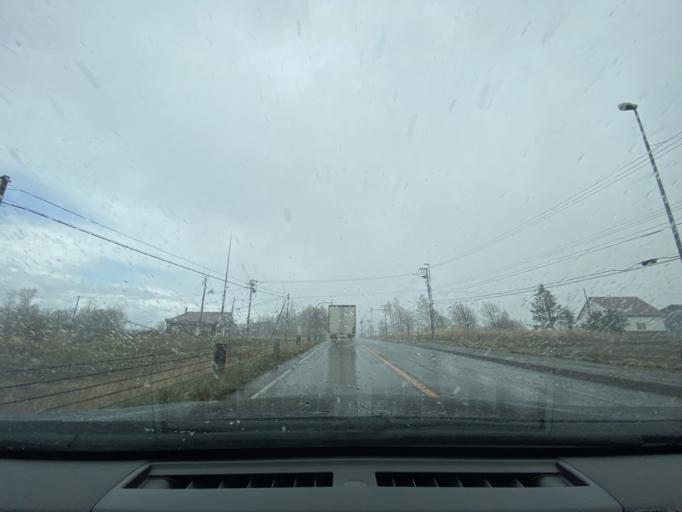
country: JP
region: Hokkaido
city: Fukagawa
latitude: 43.6472
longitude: 141.9612
